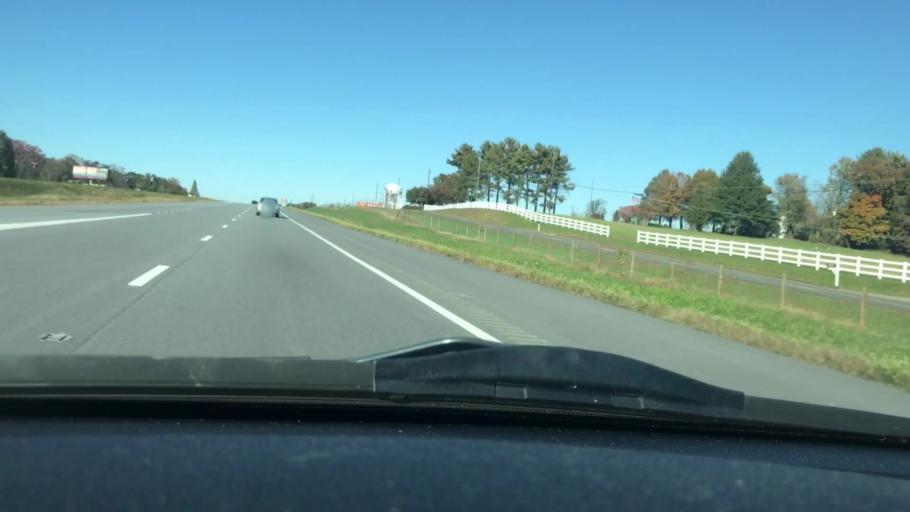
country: US
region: North Carolina
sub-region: Guilford County
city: Stokesdale
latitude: 36.2870
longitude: -79.9396
